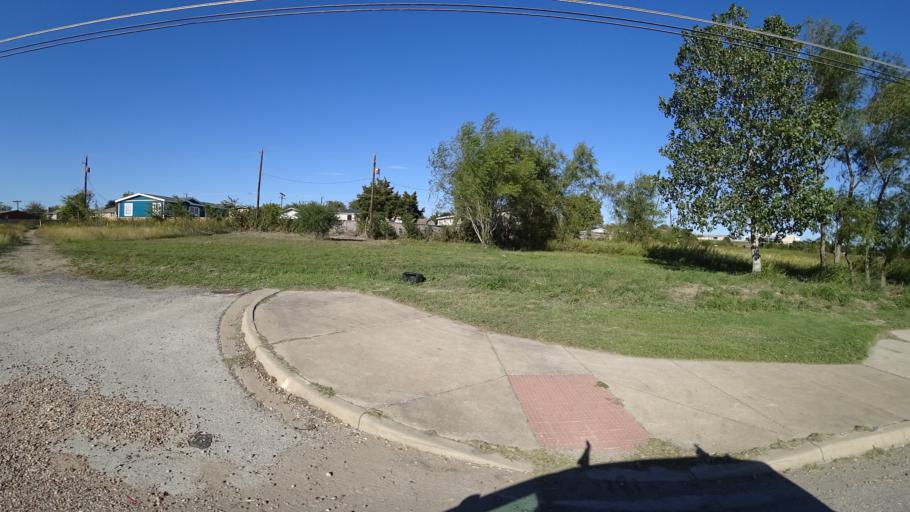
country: US
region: Texas
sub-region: Travis County
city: Hornsby Bend
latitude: 30.2923
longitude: -97.6299
